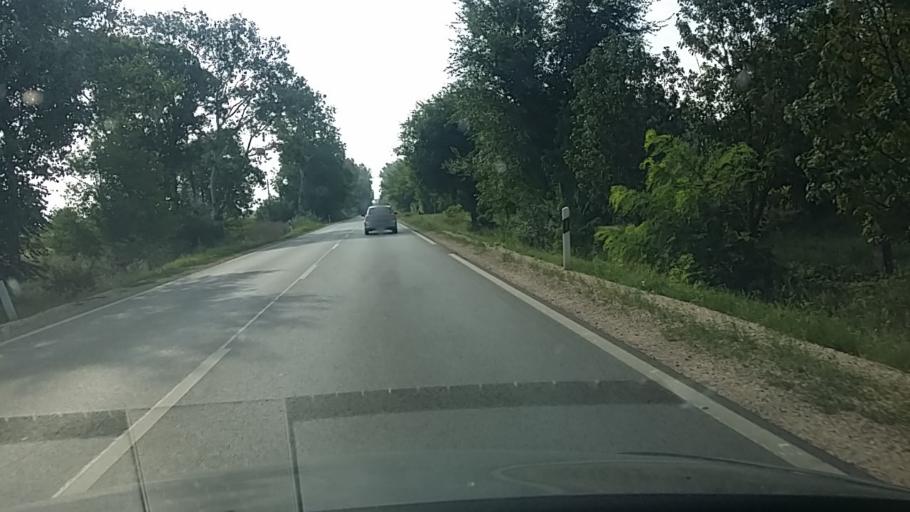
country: HU
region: Bekes
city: Szarvas
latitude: 46.8397
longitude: 20.6265
